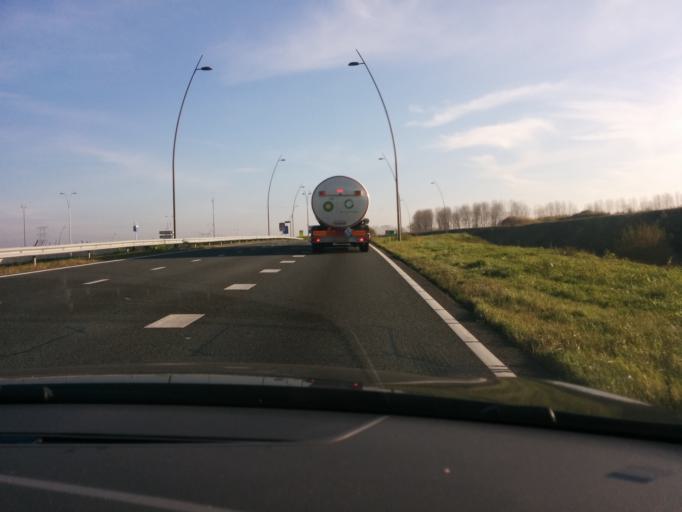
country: NL
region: North Brabant
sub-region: Gemeente Son en Breugel
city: Son
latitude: 51.4957
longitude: 5.4613
